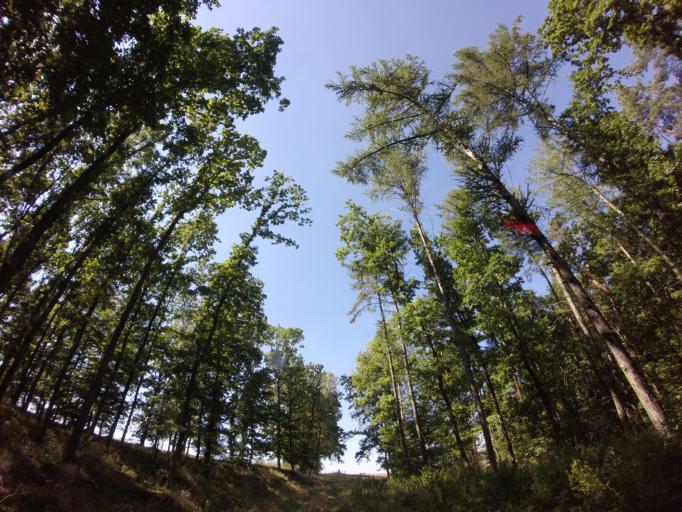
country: PL
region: West Pomeranian Voivodeship
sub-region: Powiat choszczenski
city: Recz
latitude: 53.2321
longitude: 15.6265
